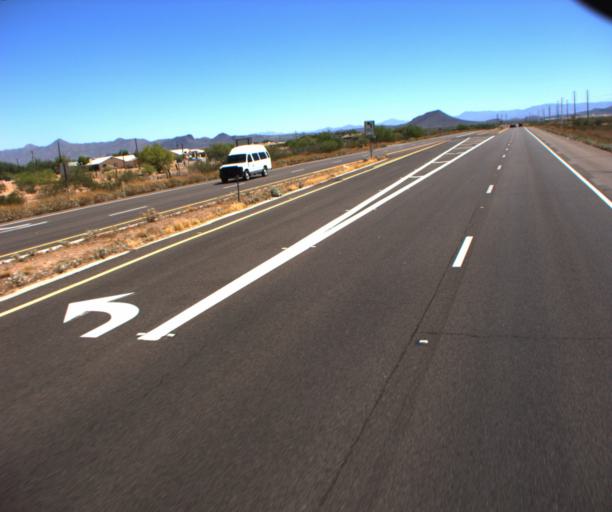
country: US
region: Arizona
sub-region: Maricopa County
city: Mesa
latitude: 33.4851
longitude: -111.8202
